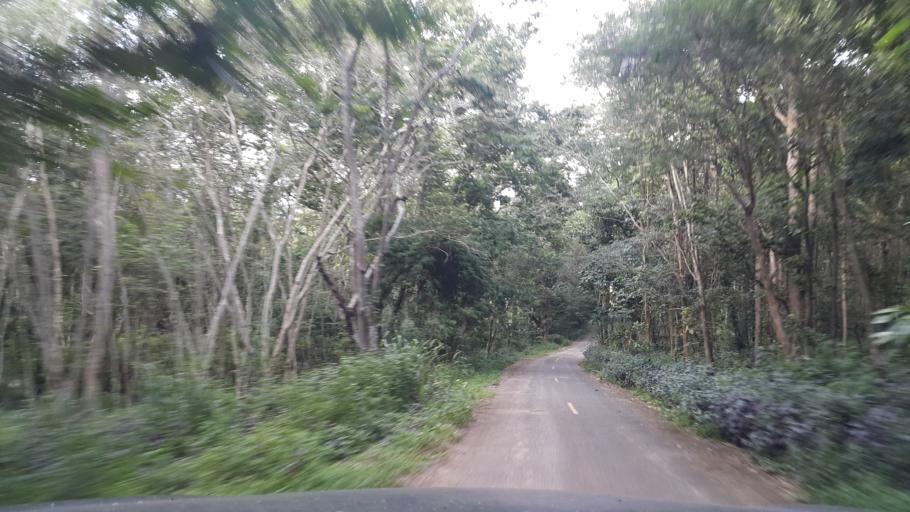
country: TH
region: Chiang Mai
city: San Sai
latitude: 18.9353
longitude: 99.0625
